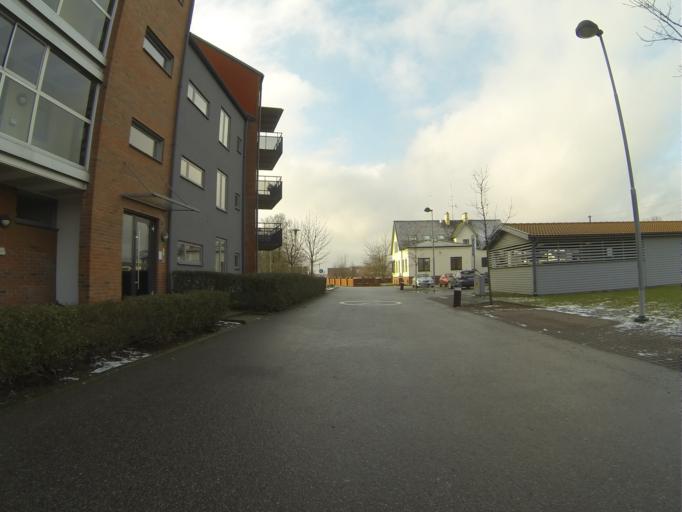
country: SE
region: Skane
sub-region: Svedala Kommun
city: Svedala
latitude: 55.5062
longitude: 13.2399
